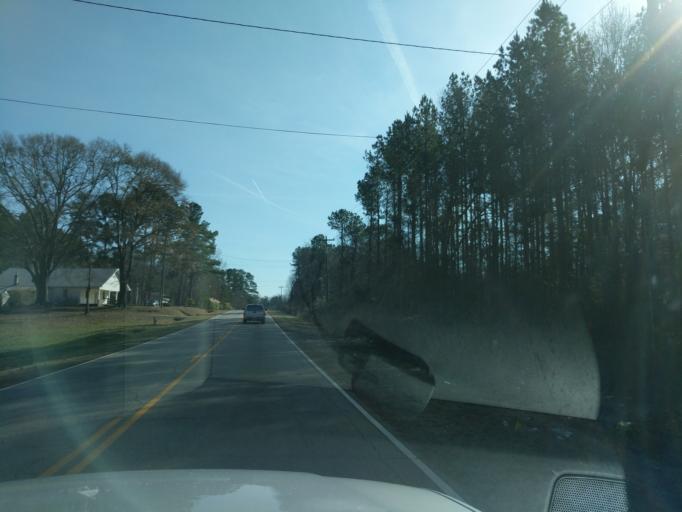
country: US
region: South Carolina
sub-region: Spartanburg County
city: Woodruff
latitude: 34.6702
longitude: -81.9715
